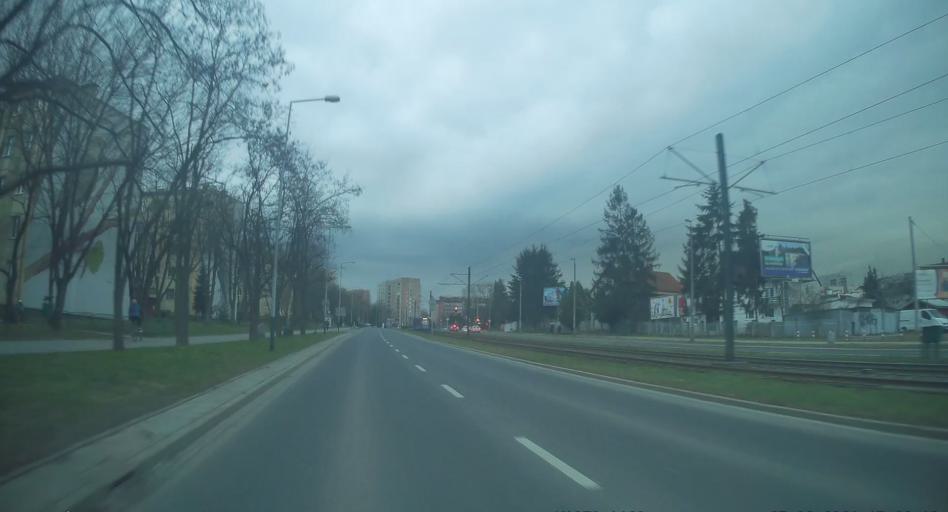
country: PL
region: Lesser Poland Voivodeship
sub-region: Krakow
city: Krakow
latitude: 50.0203
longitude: 19.9777
